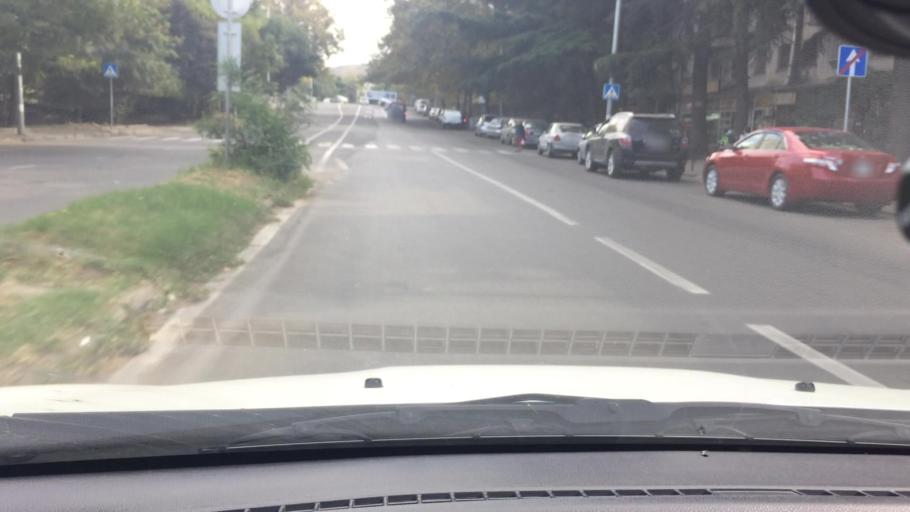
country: GE
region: T'bilisi
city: Tbilisi
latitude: 41.6732
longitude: 44.8325
